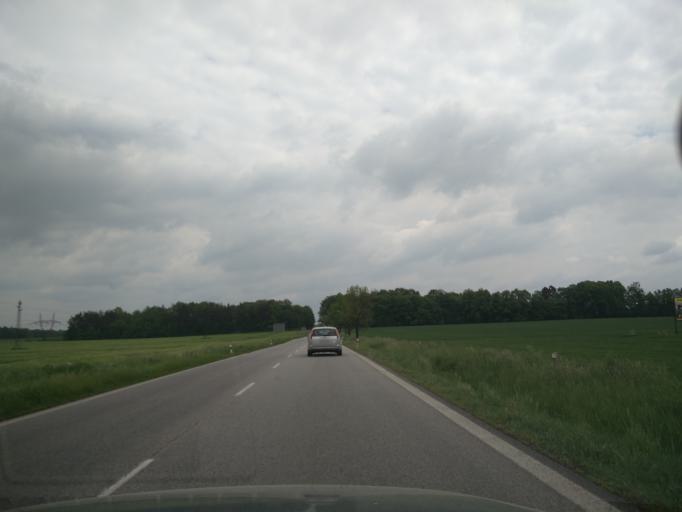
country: CZ
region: Jihocesky
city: Zliv
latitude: 49.0306
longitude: 14.3692
